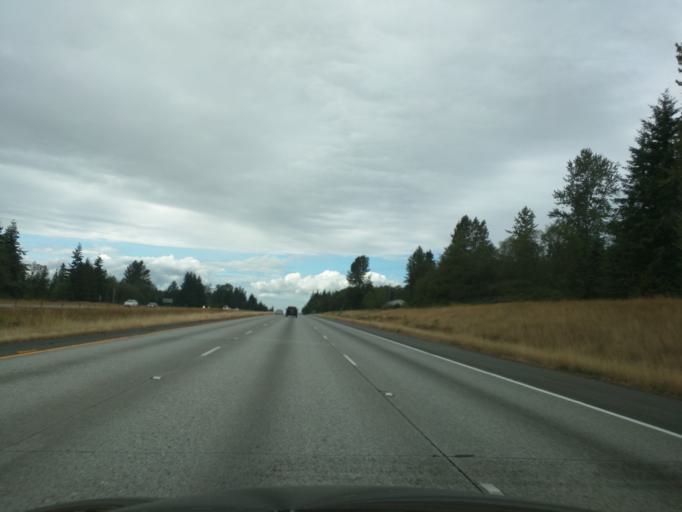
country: US
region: Washington
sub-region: Snohomish County
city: Stanwood
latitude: 48.2891
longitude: -122.2935
